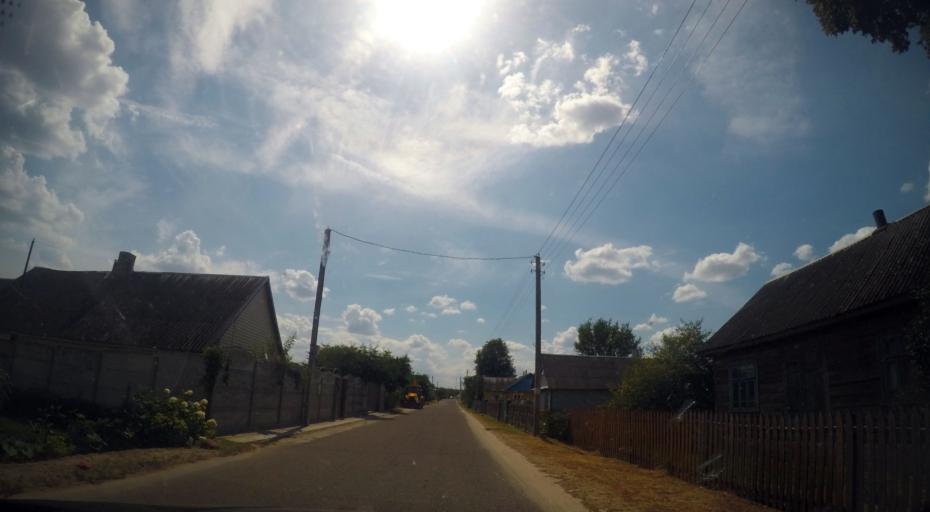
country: BY
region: Grodnenskaya
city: Hrodna
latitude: 53.6297
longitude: 23.8420
